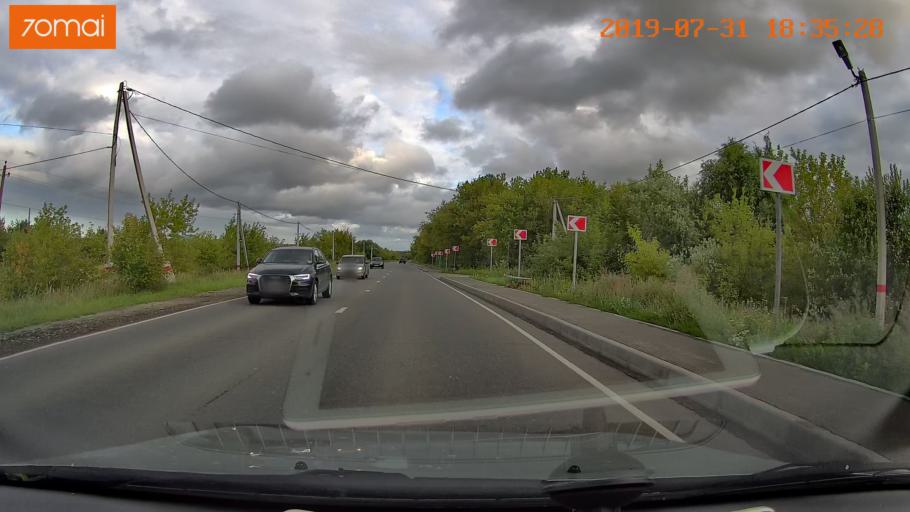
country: RU
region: Moskovskaya
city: Voskresensk
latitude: 55.2948
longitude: 38.6689
